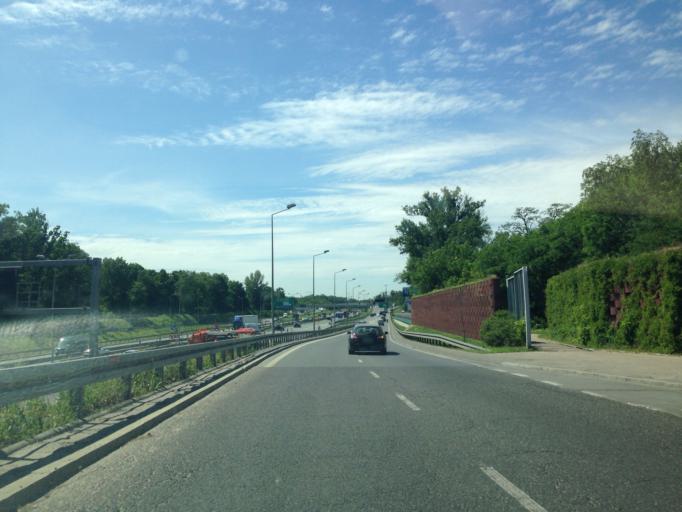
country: PL
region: Masovian Voivodeship
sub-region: Warszawa
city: Zoliborz
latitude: 52.2620
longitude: 20.9525
